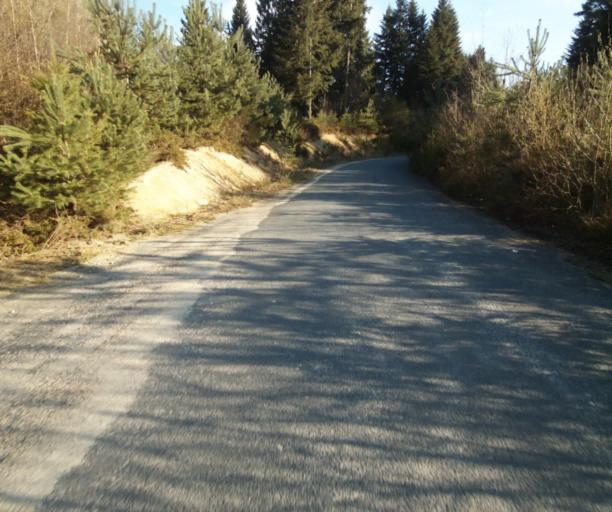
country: FR
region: Limousin
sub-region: Departement de la Correze
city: Correze
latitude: 45.3366
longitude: 1.9002
